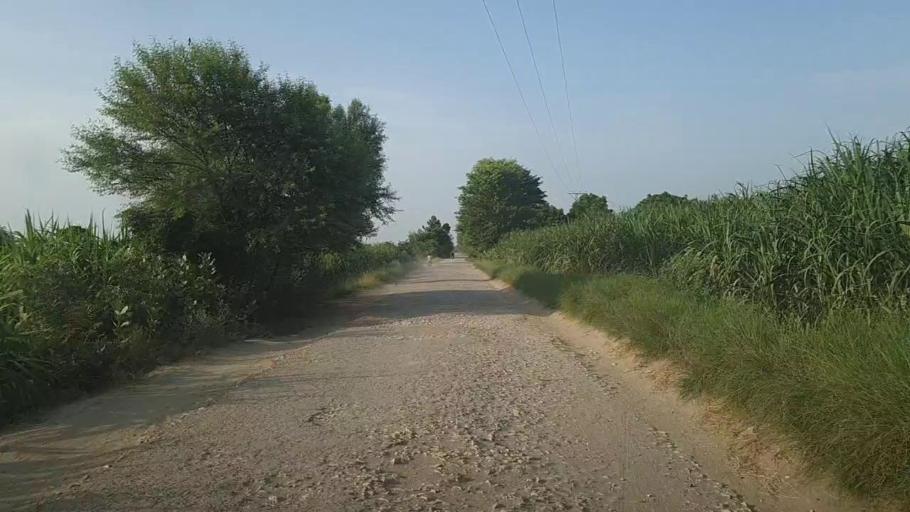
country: PK
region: Sindh
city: Ubauro
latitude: 28.3281
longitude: 69.7973
